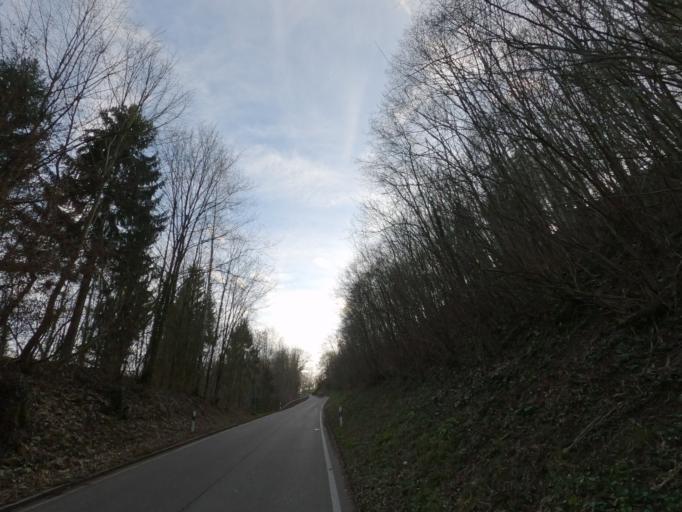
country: DE
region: Baden-Wuerttemberg
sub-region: Regierungsbezirk Stuttgart
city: Ottenbach
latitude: 48.7495
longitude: 9.7496
